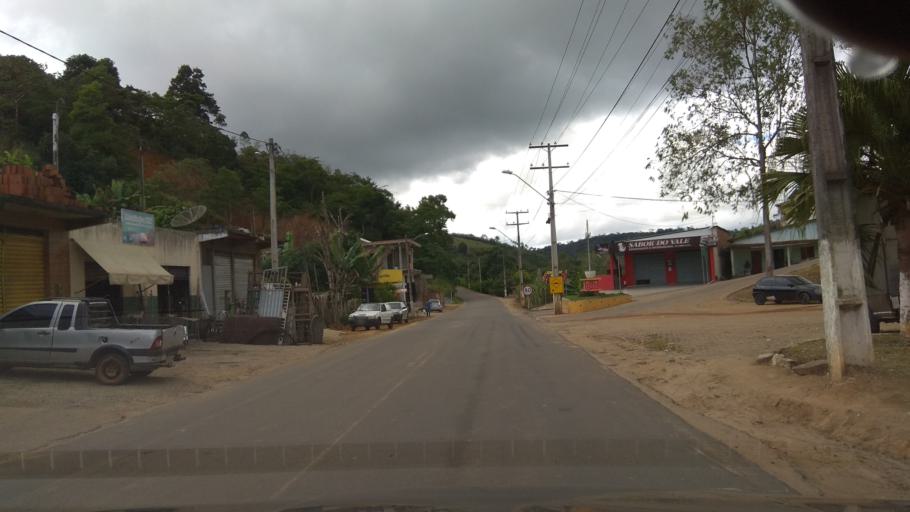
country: BR
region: Bahia
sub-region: Mutuipe
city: Mutuipe
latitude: -13.2518
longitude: -39.5683
